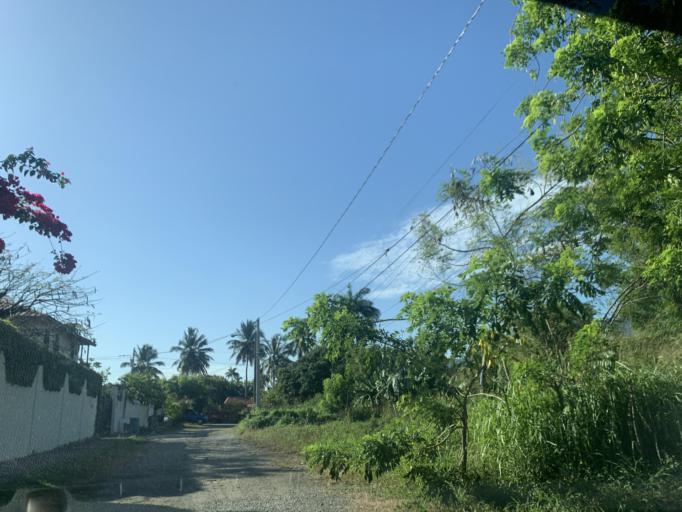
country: DO
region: Puerto Plata
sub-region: Puerto Plata
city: Puerto Plata
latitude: 19.8098
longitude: -70.7142
